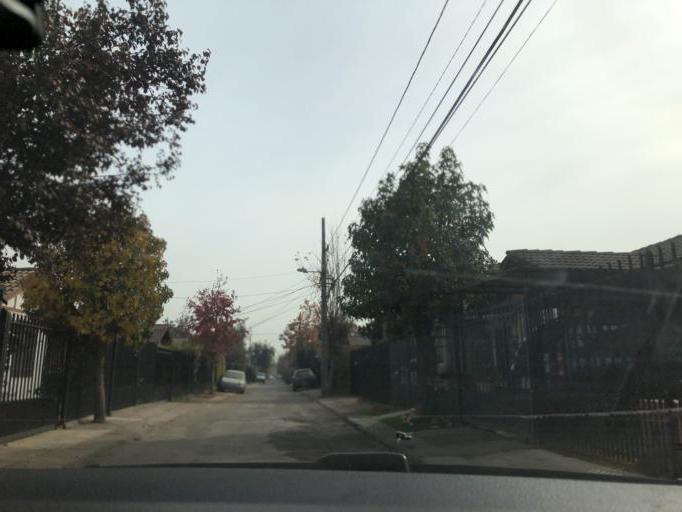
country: CL
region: Santiago Metropolitan
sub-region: Provincia de Cordillera
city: Puente Alto
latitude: -33.5517
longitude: -70.5617
